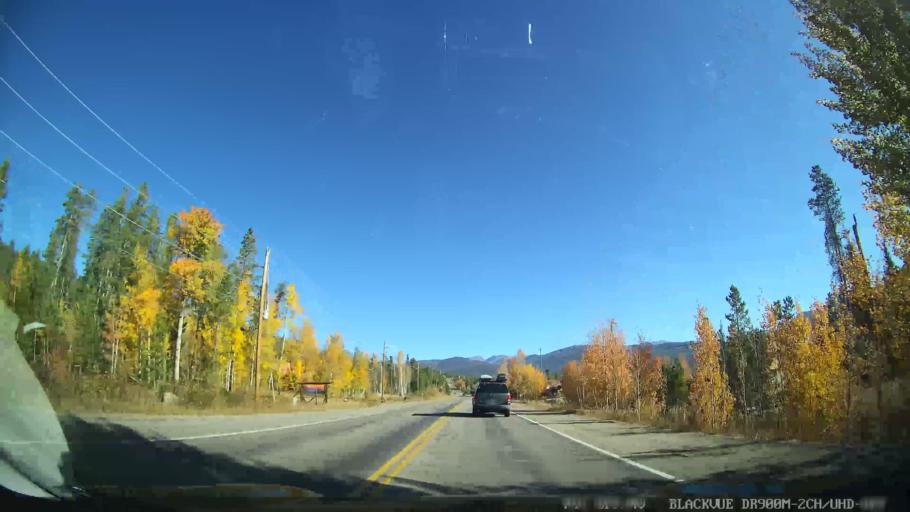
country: US
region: Colorado
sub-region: Grand County
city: Granby
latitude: 40.2321
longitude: -105.8492
